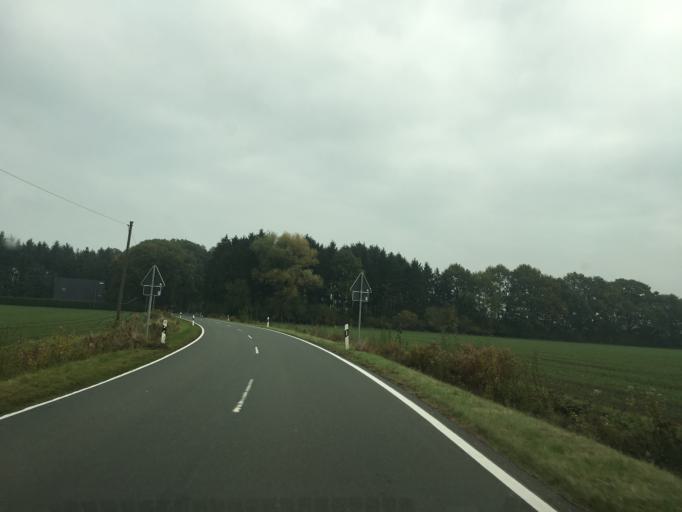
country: DE
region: North Rhine-Westphalia
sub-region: Regierungsbezirk Munster
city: Havixbeck
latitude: 51.9903
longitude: 7.4087
